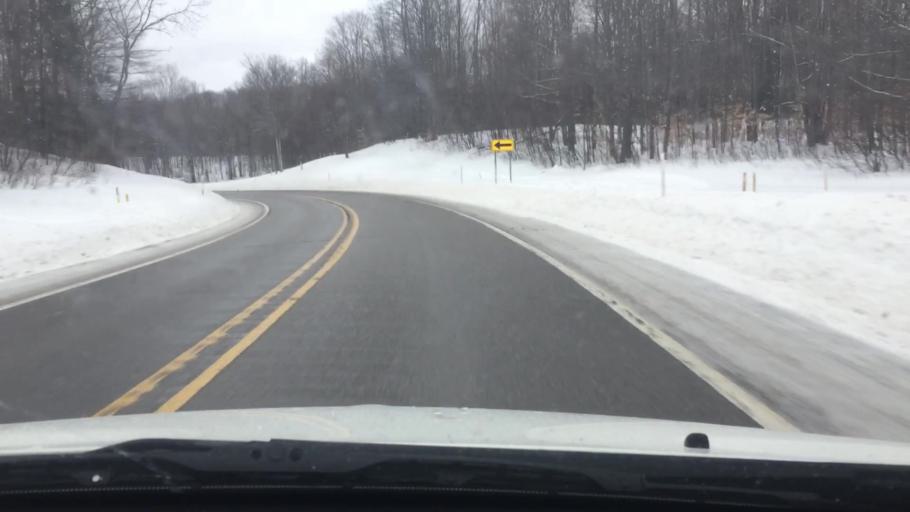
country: US
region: Michigan
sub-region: Charlevoix County
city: Boyne City
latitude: 45.0846
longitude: -84.9247
